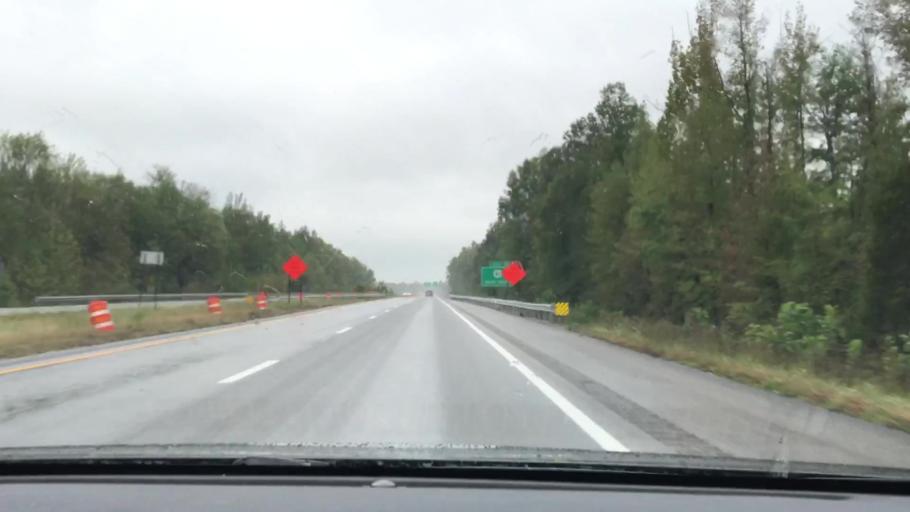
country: US
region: Kentucky
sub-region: Hopkins County
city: Nortonville
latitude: 37.1599
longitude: -87.4586
